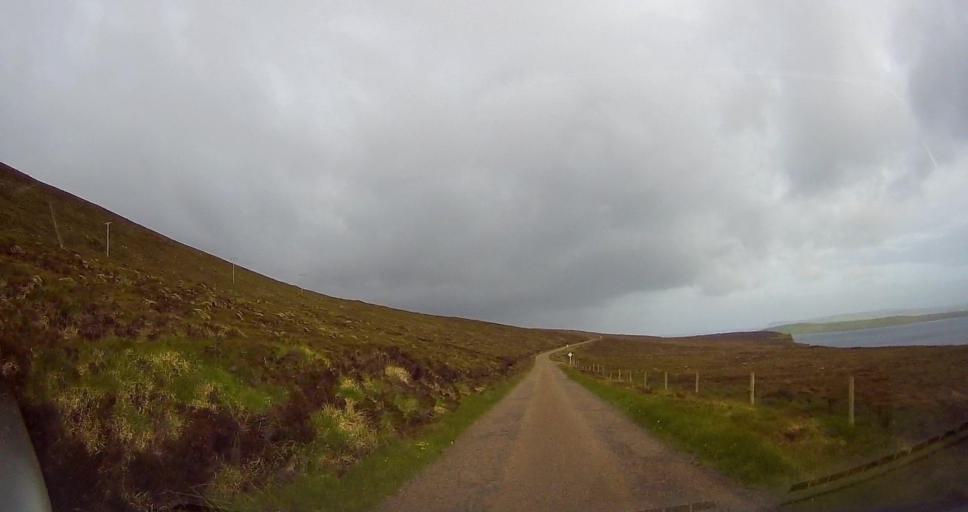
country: GB
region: Scotland
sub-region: Orkney Islands
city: Stromness
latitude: 58.8904
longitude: -3.2580
